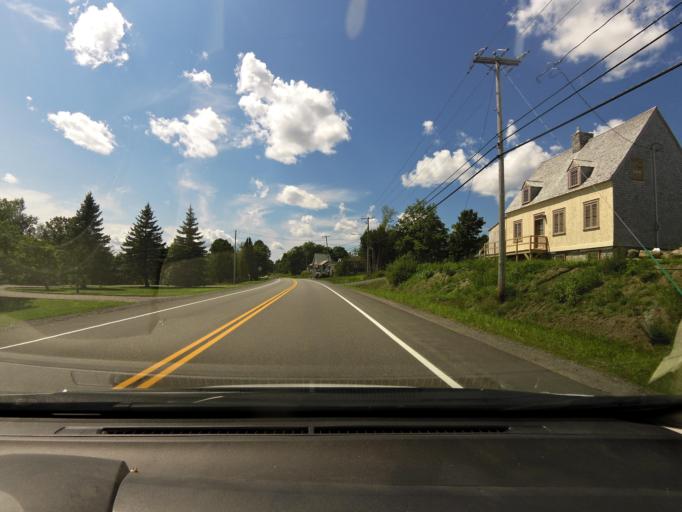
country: CA
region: Quebec
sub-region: Capitale-Nationale
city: Neuville
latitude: 46.7132
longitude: -71.5571
